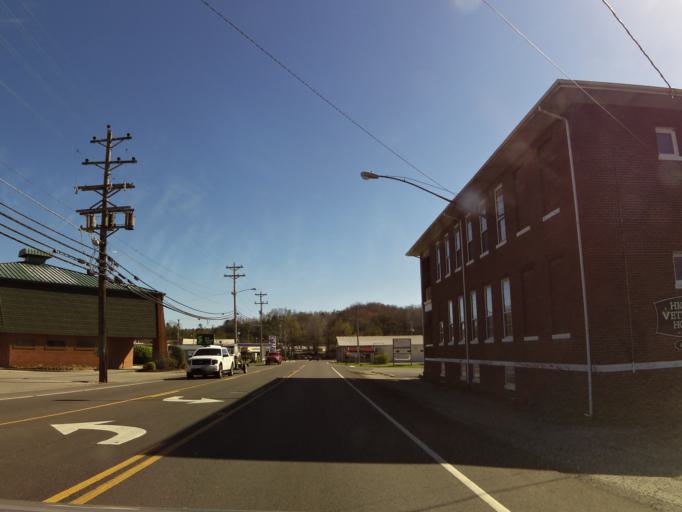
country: US
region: Tennessee
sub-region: Scott County
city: Oneida
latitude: 36.4993
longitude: -84.5162
